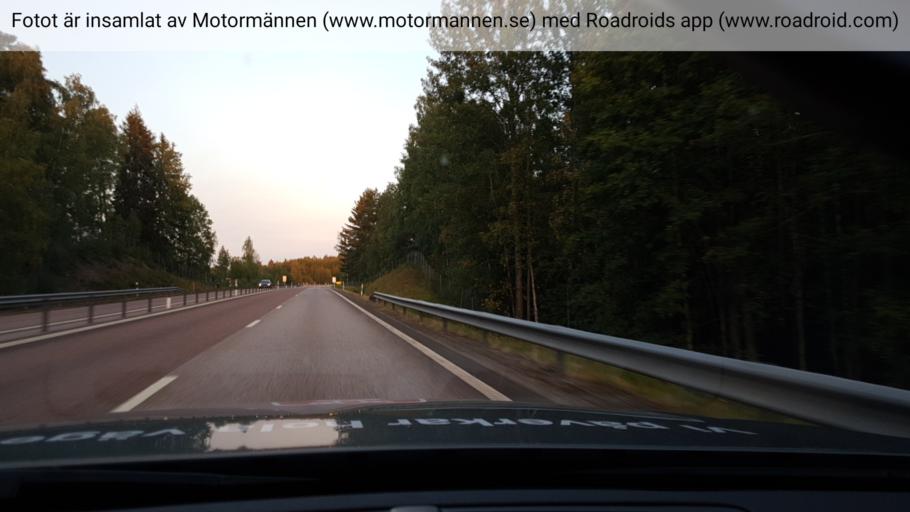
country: SE
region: Vaestmanland
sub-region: Norbergs Kommun
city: Norberg
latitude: 59.9067
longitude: 15.9678
